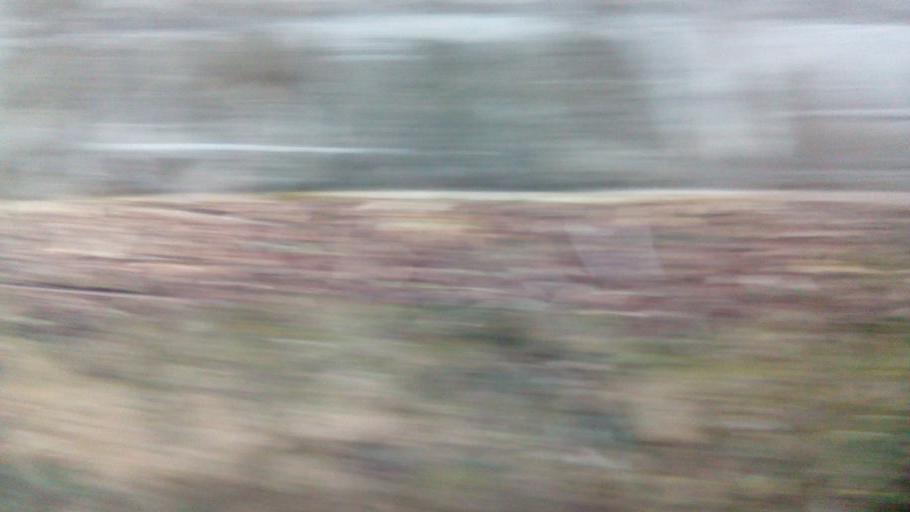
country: TW
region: Taiwan
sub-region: Hualien
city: Hualian
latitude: 24.3371
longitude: 121.3107
